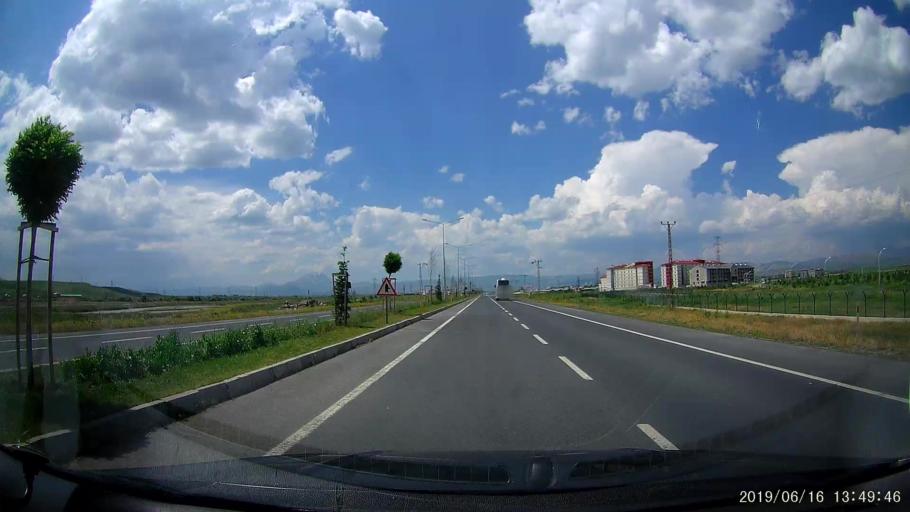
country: TR
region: Agri
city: Agri
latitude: 39.7202
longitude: 42.9867
